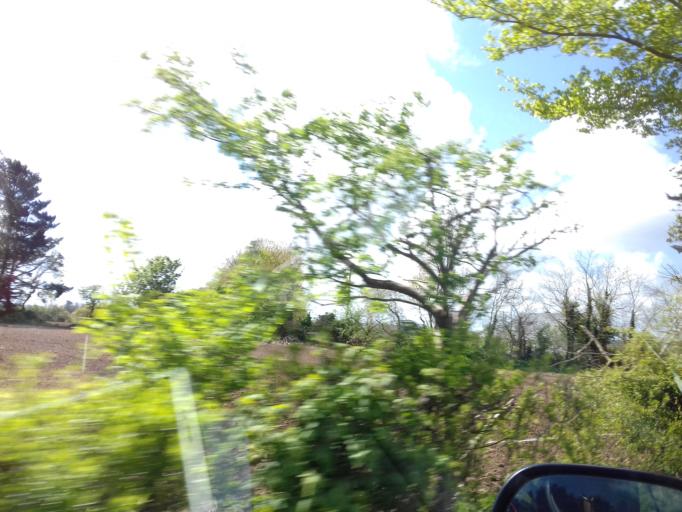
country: IE
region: Leinster
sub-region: Loch Garman
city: Castlebridge
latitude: 52.3699
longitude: -6.4375
